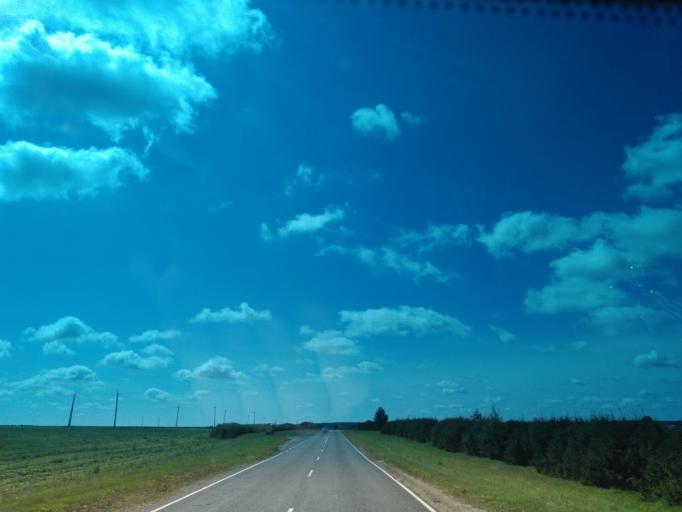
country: BY
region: Minsk
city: Uzda
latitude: 53.3777
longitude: 27.2376
